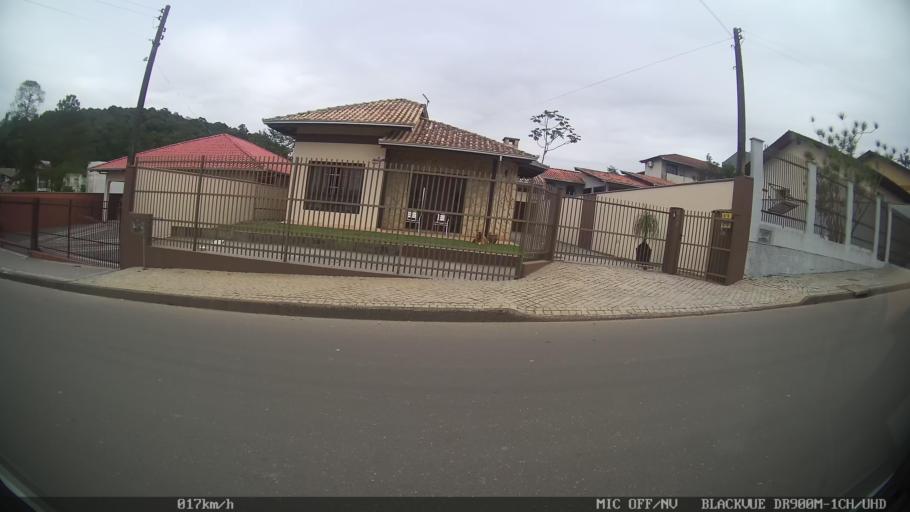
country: BR
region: Santa Catarina
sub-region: Joinville
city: Joinville
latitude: -26.2705
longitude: -48.8835
